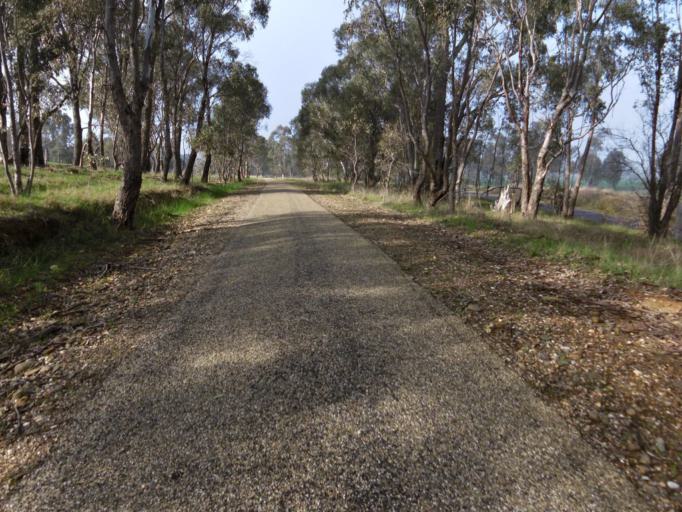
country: AU
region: Victoria
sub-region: Wangaratta
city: Wangaratta
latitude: -36.4487
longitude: 146.5516
